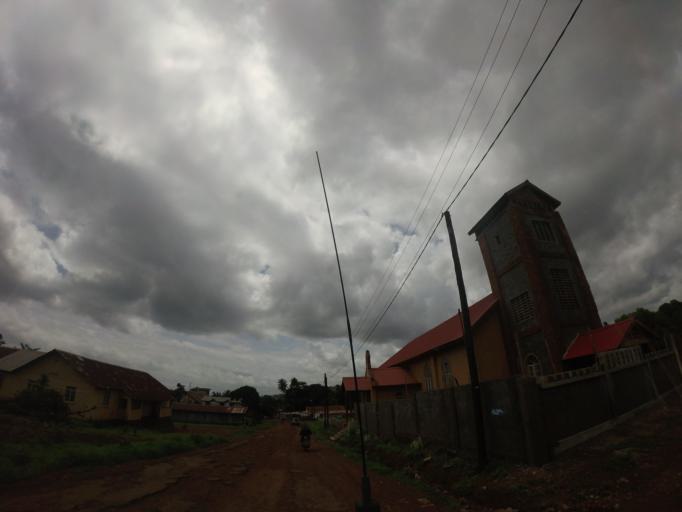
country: SL
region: Western Area
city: Hastings
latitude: 8.3799
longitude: -13.1383
